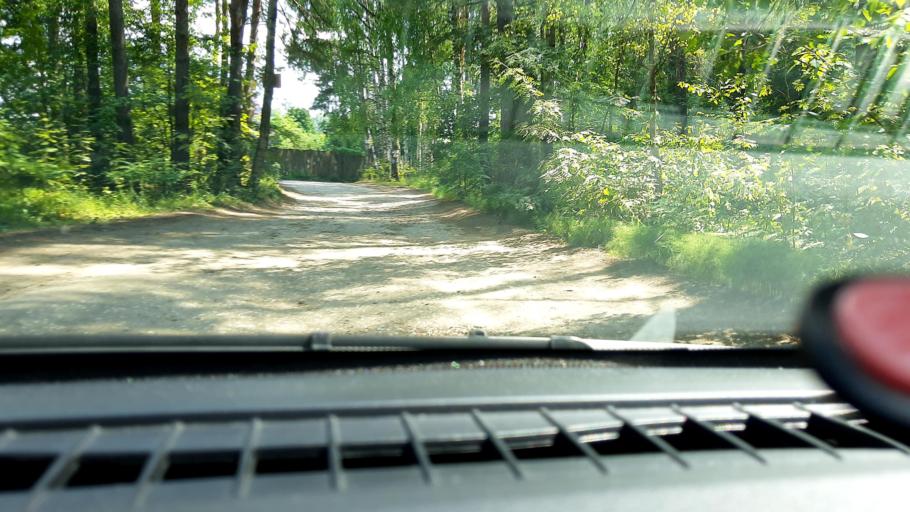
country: RU
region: Nizjnij Novgorod
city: Neklyudovo
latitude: 56.4498
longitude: 44.0002
